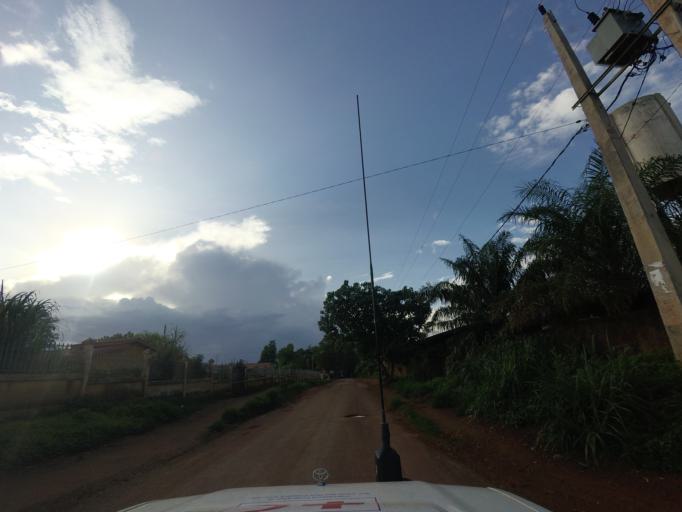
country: GN
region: Nzerekore
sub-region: Nzerekore Prefecture
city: Nzerekore
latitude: 7.7323
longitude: -8.8287
